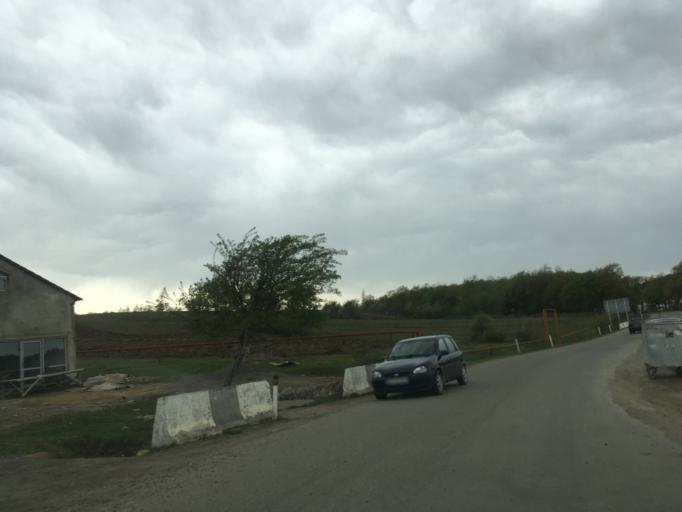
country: GE
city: Surami
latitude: 42.2375
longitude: 43.4743
